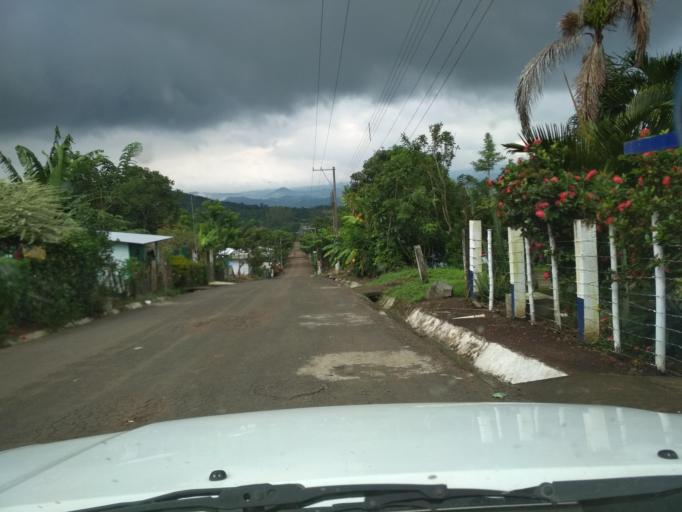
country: MX
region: Veracruz
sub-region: San Andres Tuxtla
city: El Huidero
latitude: 18.3851
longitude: -95.1785
